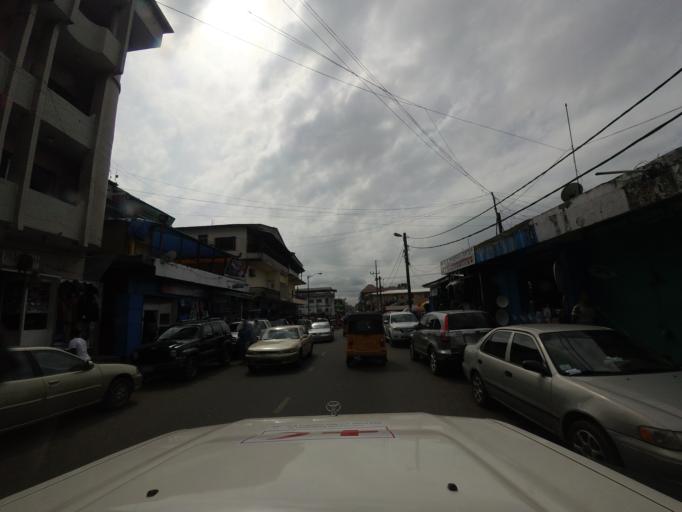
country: LR
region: Montserrado
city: Monrovia
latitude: 6.3167
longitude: -10.8076
